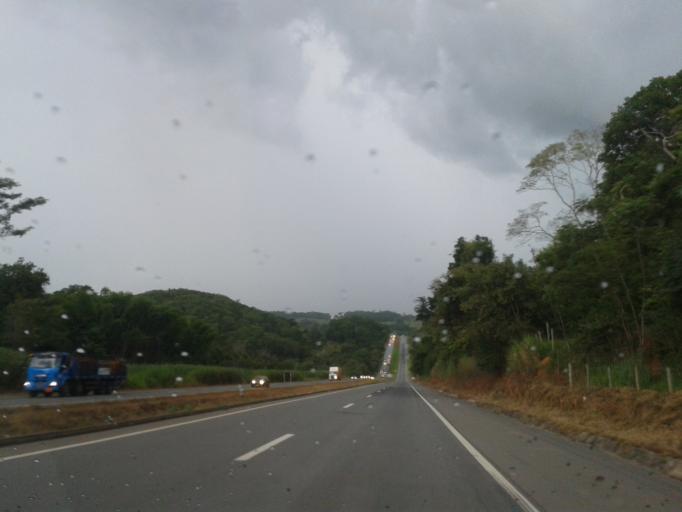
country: BR
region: Goias
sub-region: Morrinhos
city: Morrinhos
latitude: -17.5873
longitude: -49.1940
